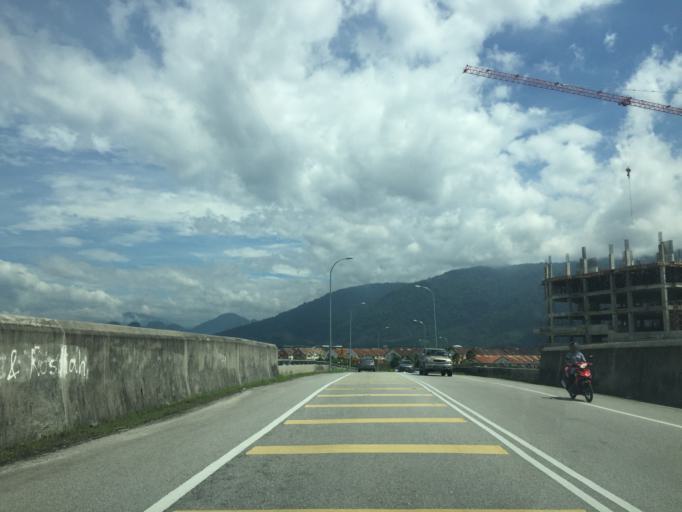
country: MY
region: Perak
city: Kampar
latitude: 4.3273
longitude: 101.1311
